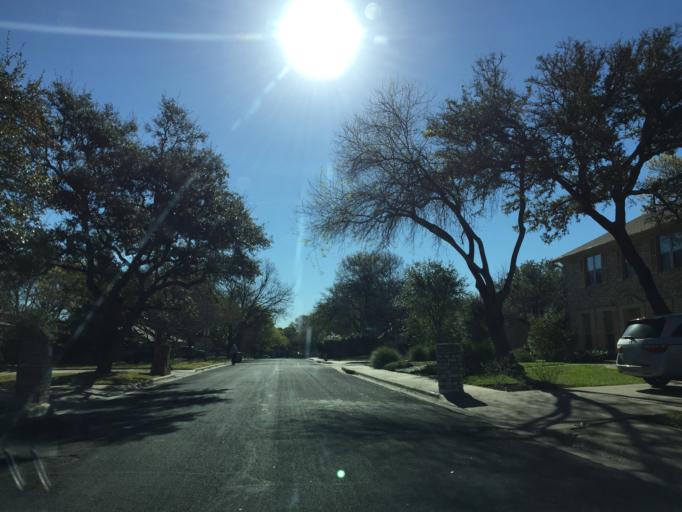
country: US
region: Texas
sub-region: Williamson County
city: Jollyville
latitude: 30.4076
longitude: -97.7351
